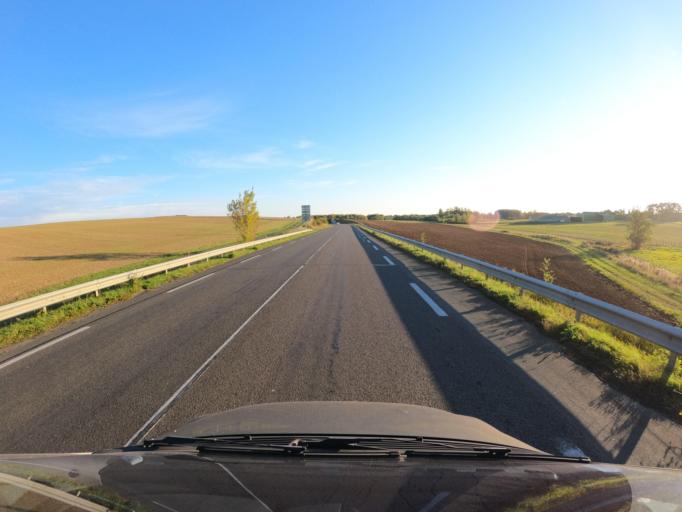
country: FR
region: Pays de la Loire
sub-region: Departement de la Vendee
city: Sainte-Hermine
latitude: 46.5629
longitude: -1.0468
